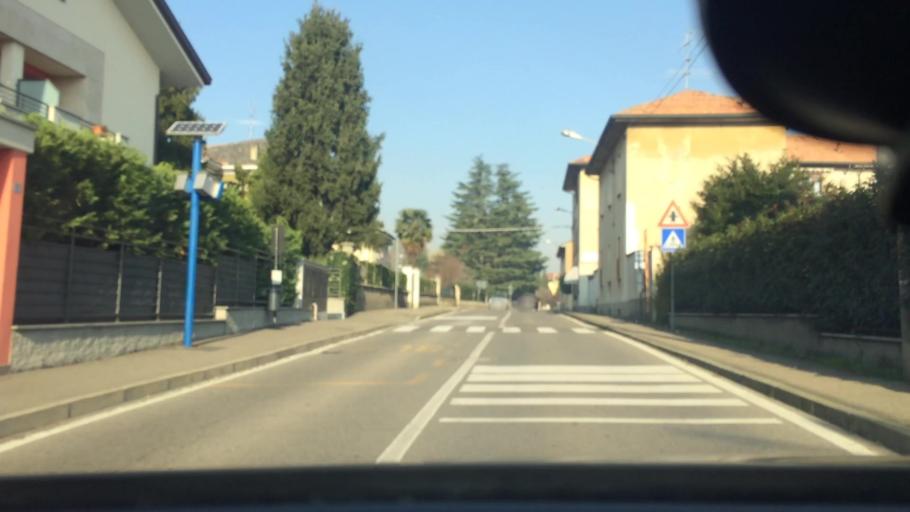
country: IT
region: Lombardy
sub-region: Provincia di Monza e Brianza
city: Misinto
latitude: 45.6650
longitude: 9.0832
